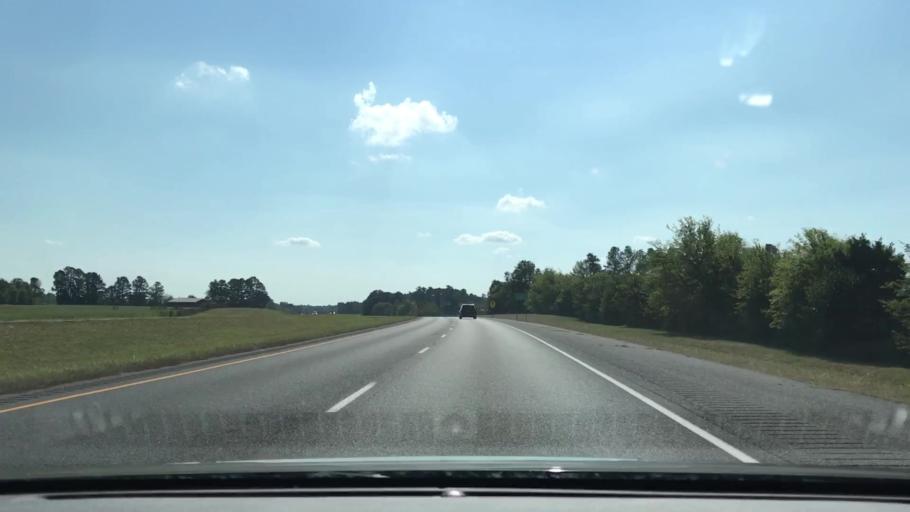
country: US
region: Kentucky
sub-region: Marshall County
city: Benton
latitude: 36.7964
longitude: -88.3377
